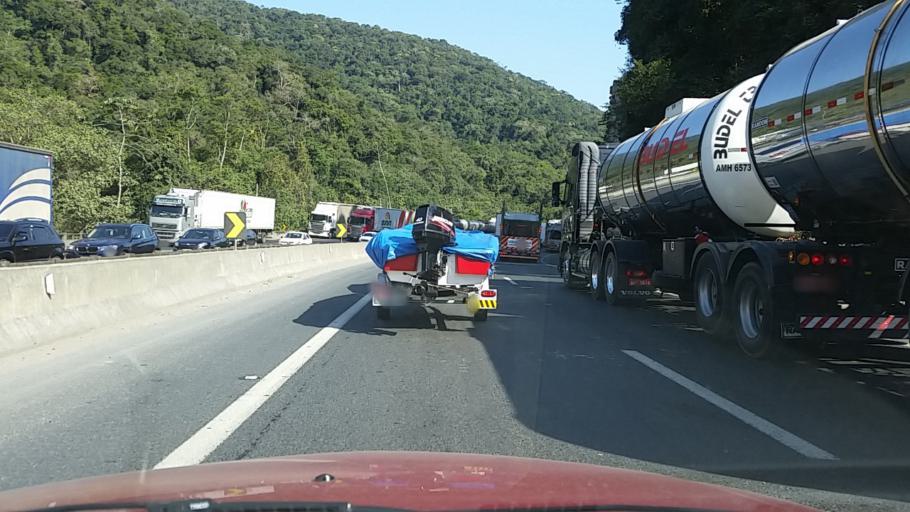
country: BR
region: Sao Paulo
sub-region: Juquitiba
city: Juquitiba
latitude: -24.0804
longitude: -47.2517
